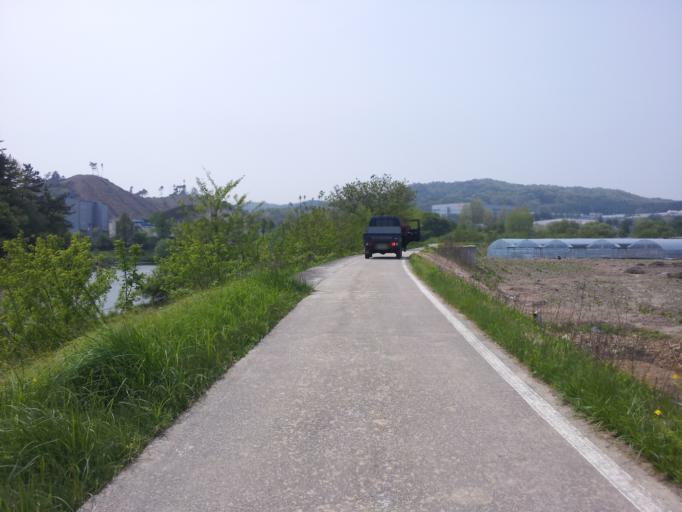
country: KR
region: Daejeon
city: Daejeon
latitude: 36.2569
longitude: 127.2844
